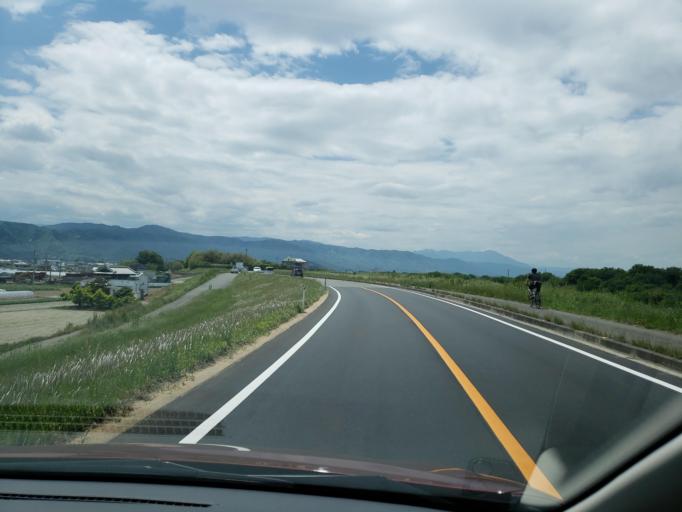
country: JP
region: Tokushima
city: Ishii
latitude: 34.0941
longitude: 134.4174
